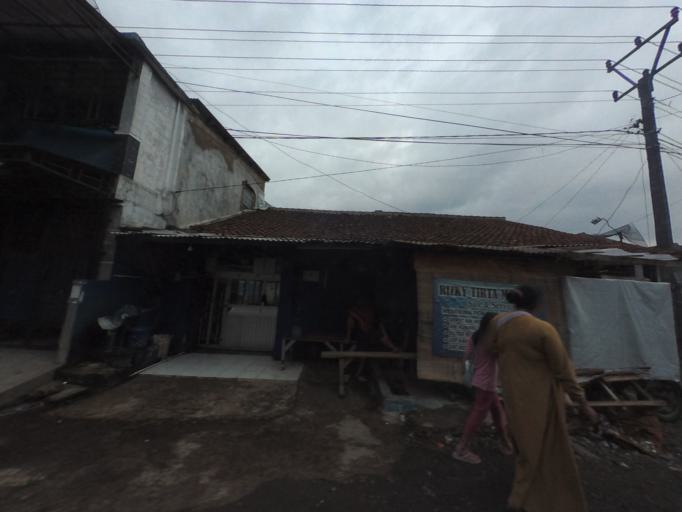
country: ID
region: West Java
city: Cicurug
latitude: -6.8354
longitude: 106.7603
